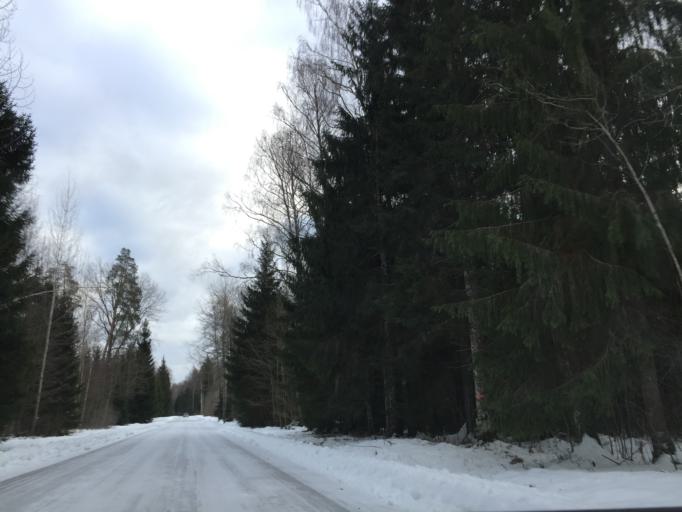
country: LV
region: Lielvarde
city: Lielvarde
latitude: 56.5831
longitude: 24.7447
